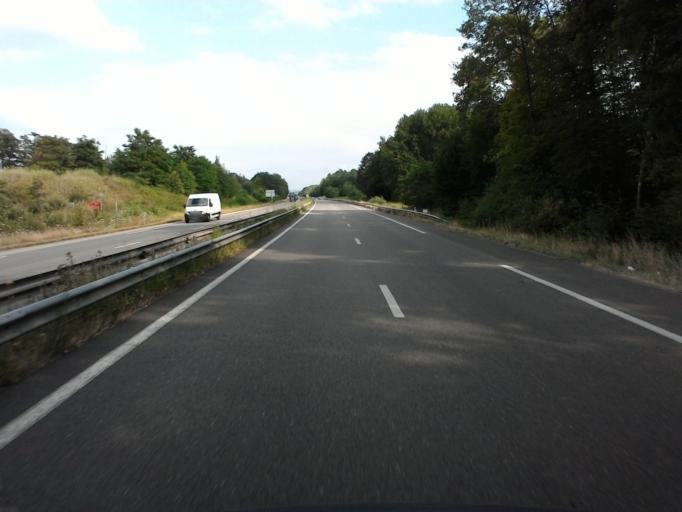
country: FR
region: Lorraine
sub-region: Departement des Vosges
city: Thaon-les-Vosges
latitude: 48.2472
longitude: 6.4032
